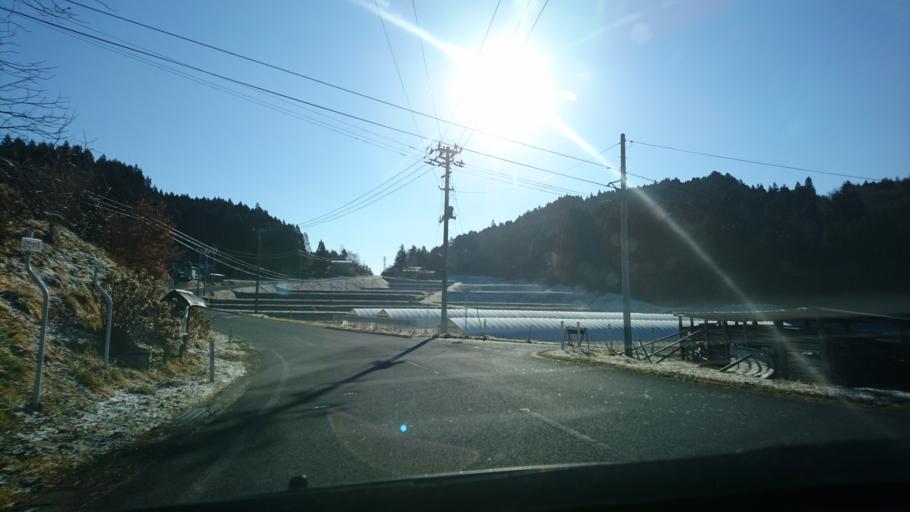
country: JP
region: Iwate
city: Ichinoseki
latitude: 38.8784
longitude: 141.3216
